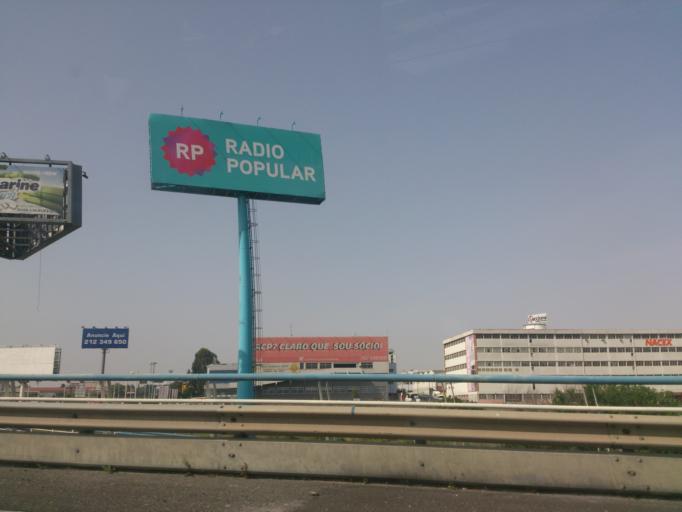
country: PT
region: Lisbon
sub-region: Loures
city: Sacavem
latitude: 38.7894
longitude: -9.1162
